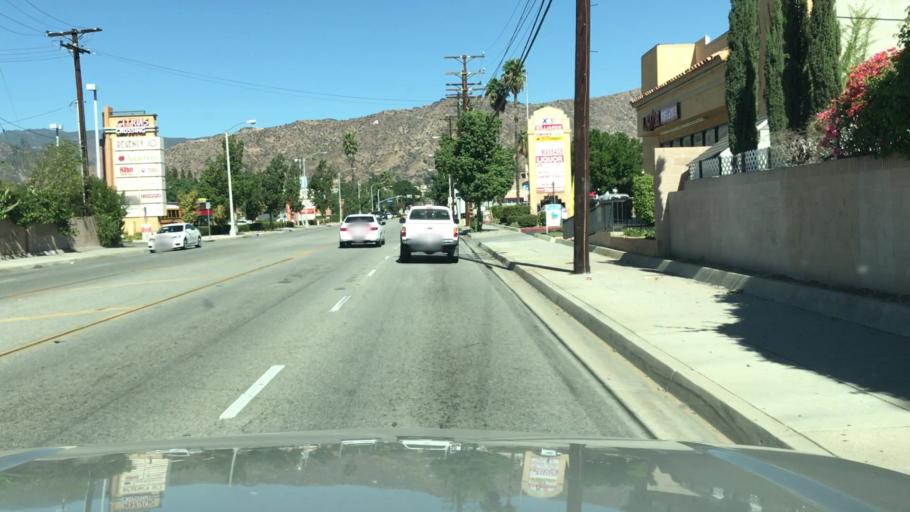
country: US
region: California
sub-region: Los Angeles County
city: Citrus
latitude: 34.1261
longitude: -117.8900
